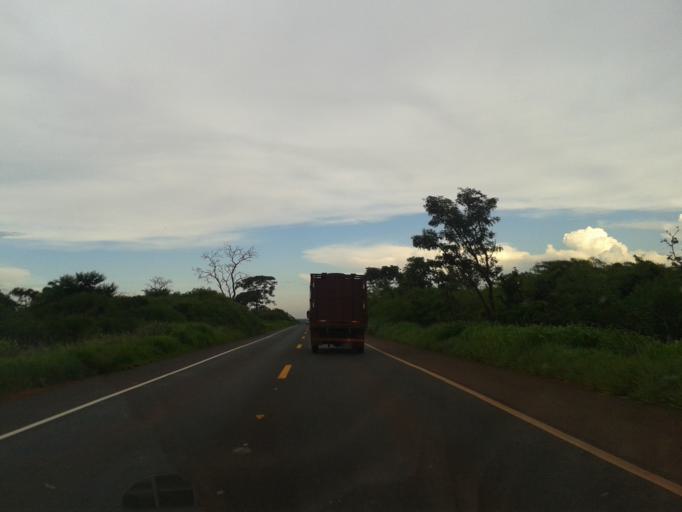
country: BR
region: Minas Gerais
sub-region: Santa Vitoria
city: Santa Vitoria
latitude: -18.8846
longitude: -50.1460
